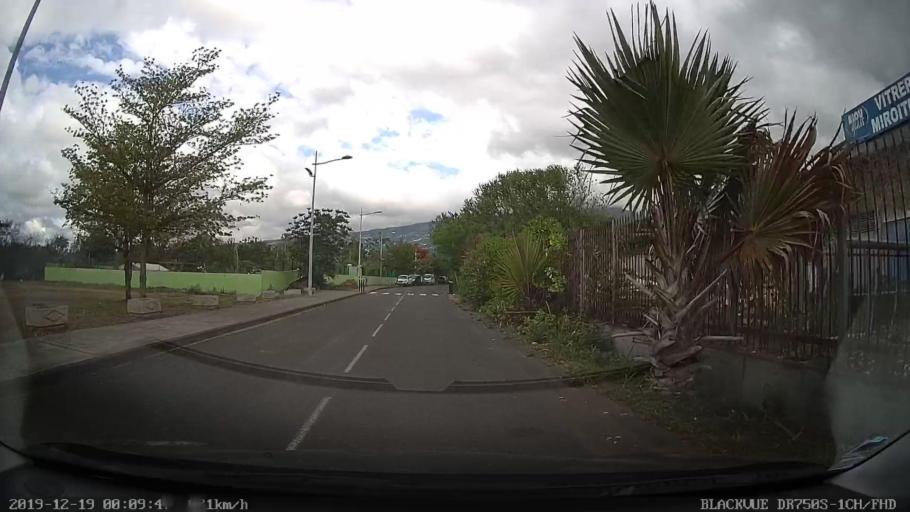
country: RE
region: Reunion
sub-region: Reunion
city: Sainte-Marie
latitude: -20.8978
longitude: 55.5033
